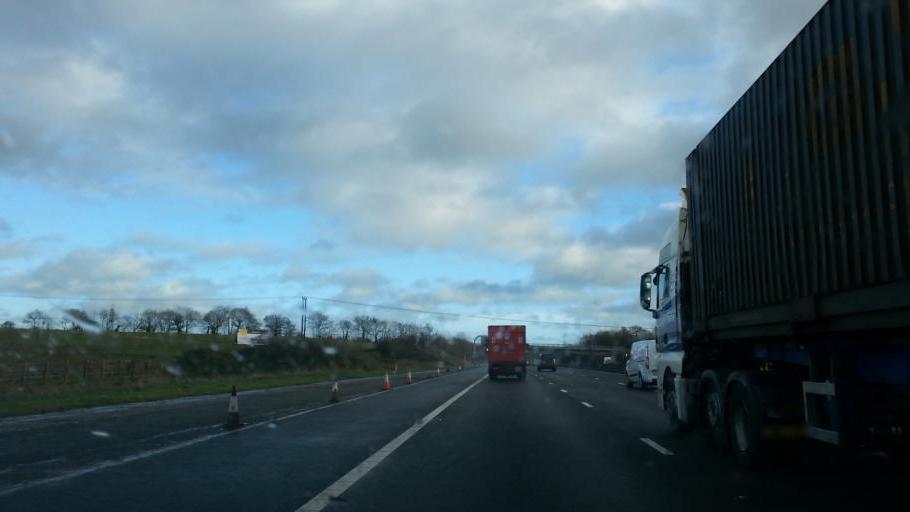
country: GB
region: England
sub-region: South Gloucestershire
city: Pucklechurch
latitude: 51.4980
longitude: -2.4146
